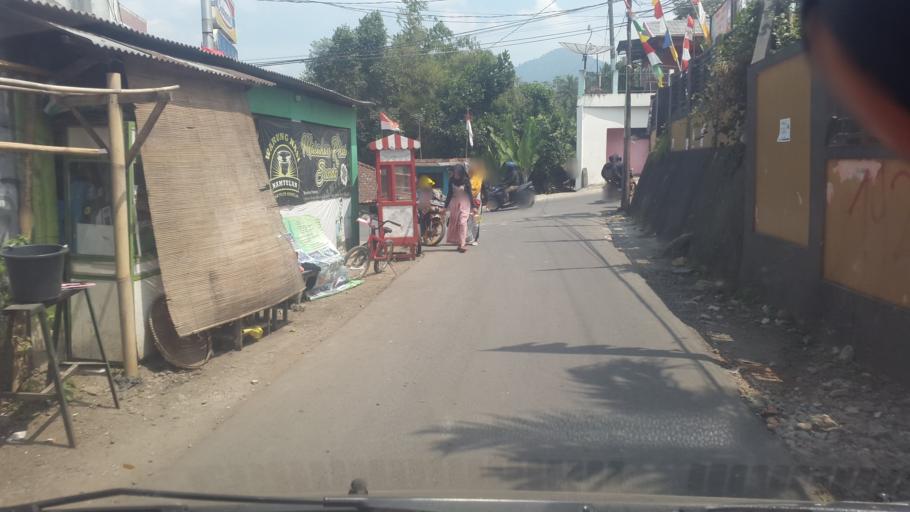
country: ID
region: West Java
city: Cicurug
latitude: -6.7736
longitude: 106.7275
